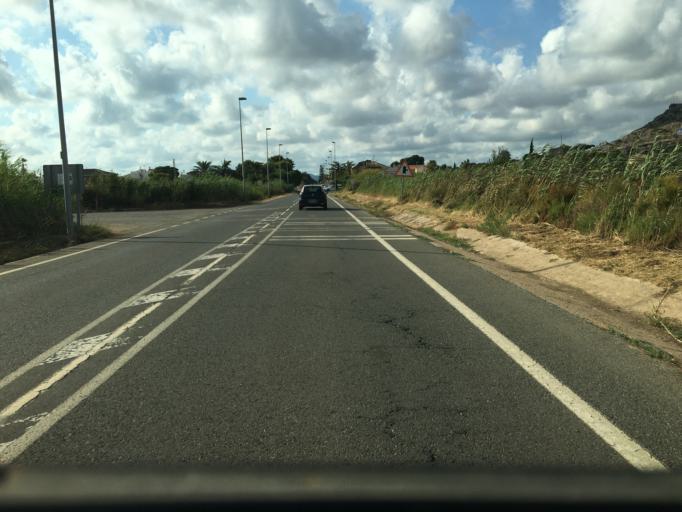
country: ES
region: Murcia
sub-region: Murcia
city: Los Alcazares
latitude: 37.6968
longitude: -0.8432
